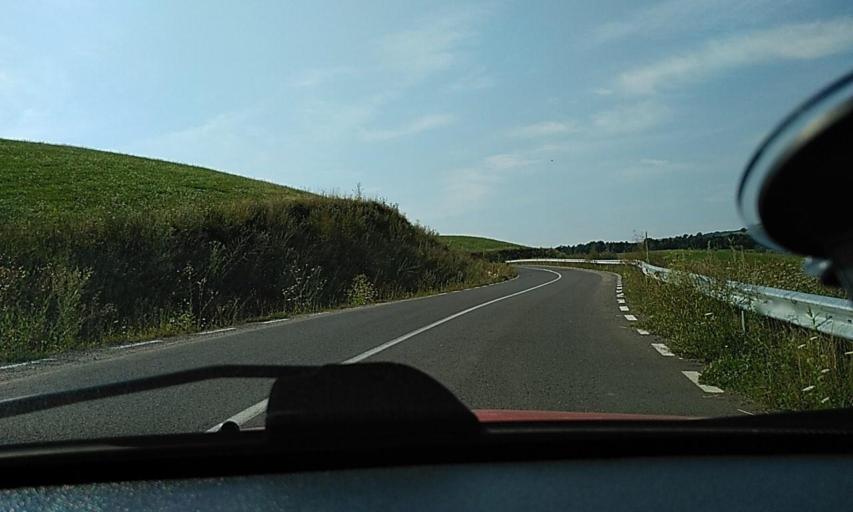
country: RO
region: Brasov
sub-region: Comuna Bunesti
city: Bunesti
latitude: 46.0672
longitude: 25.0797
